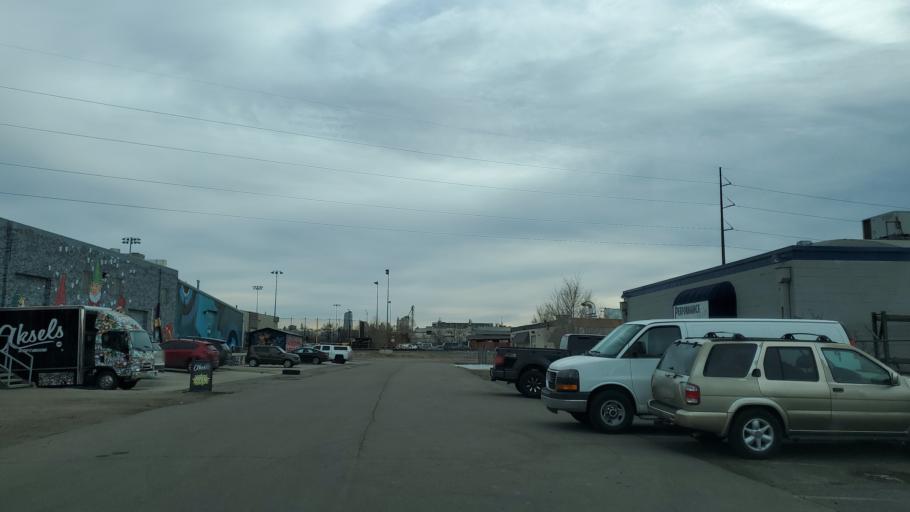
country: US
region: Colorado
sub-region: Denver County
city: Denver
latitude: 39.7130
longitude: -105.0056
